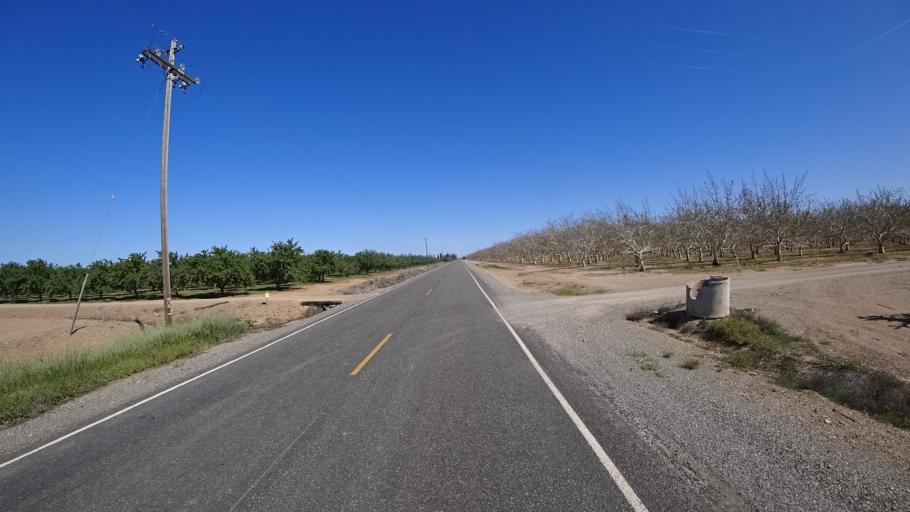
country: US
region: California
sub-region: Glenn County
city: Hamilton City
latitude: 39.6450
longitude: -122.1038
